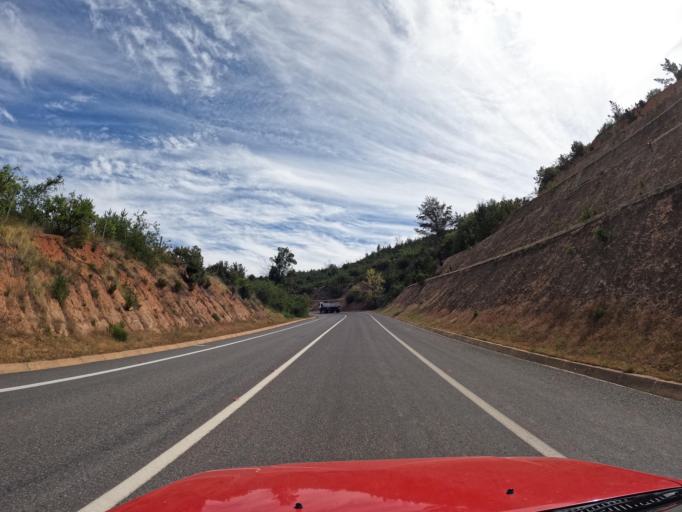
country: CL
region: Maule
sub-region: Provincia de Talca
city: Talca
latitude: -35.1636
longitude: -71.9719
